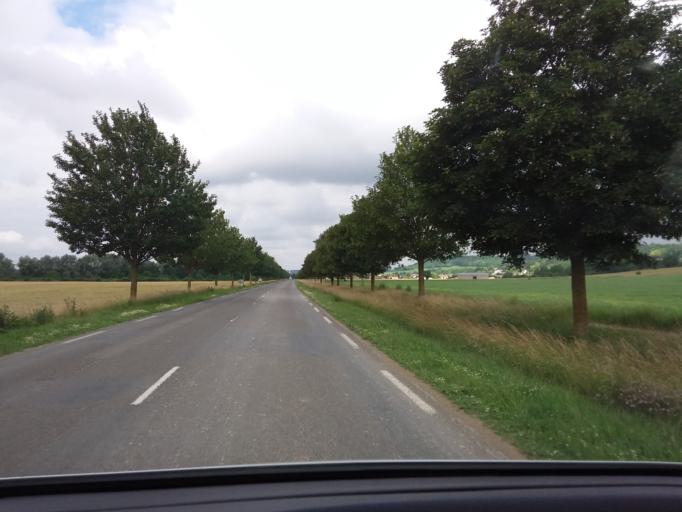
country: FR
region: Picardie
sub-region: Departement de l'Aisne
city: Bucy-le-Long
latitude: 49.3832
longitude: 3.4108
